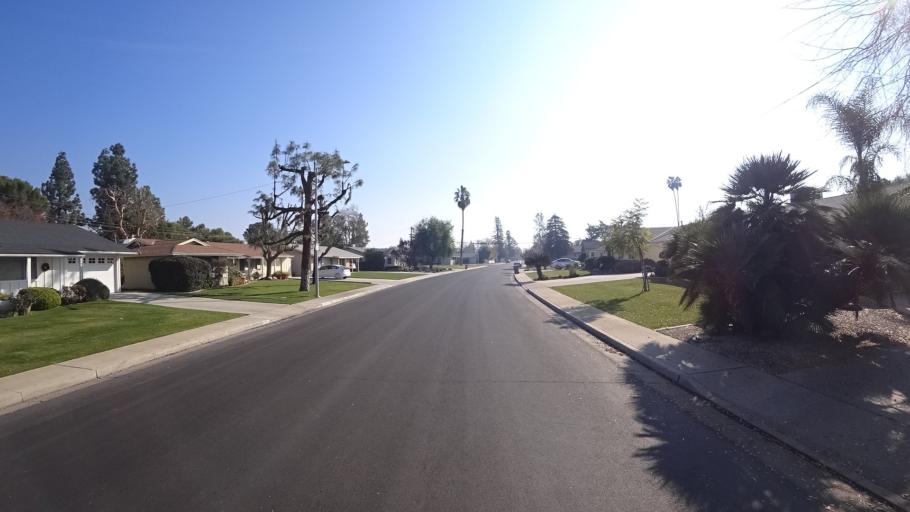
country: US
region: California
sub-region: Kern County
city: Bakersfield
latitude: 35.3503
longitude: -119.0657
